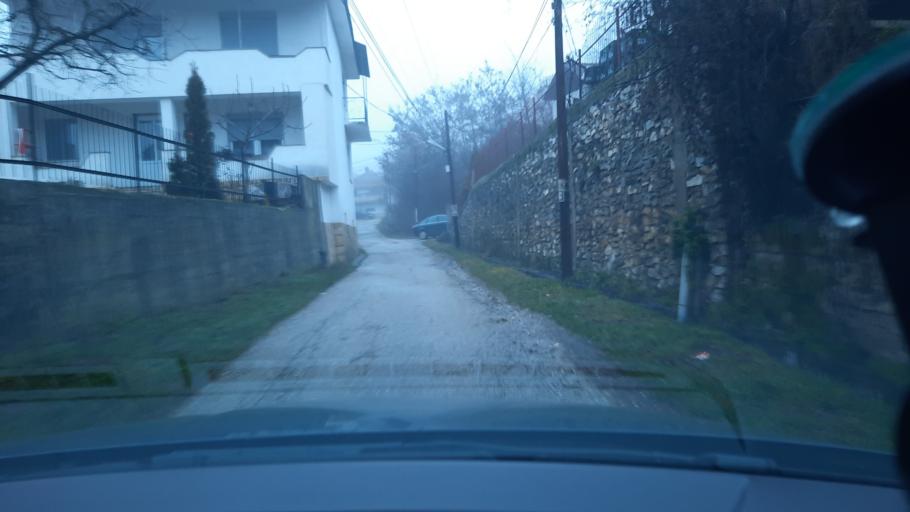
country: MK
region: Vrapciste
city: Vrapciste
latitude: 41.8401
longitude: 20.8793
